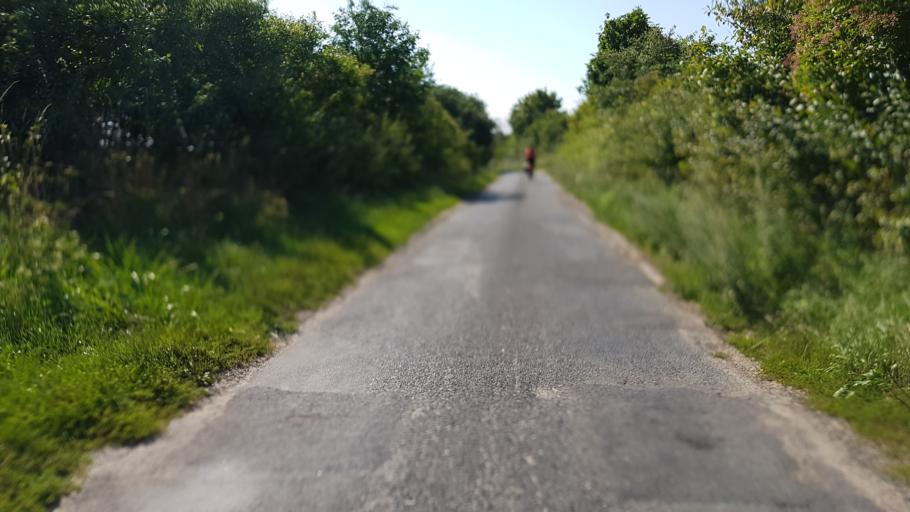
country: PL
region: West Pomeranian Voivodeship
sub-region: Powiat gryfinski
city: Gryfino
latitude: 53.1641
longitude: 14.4735
